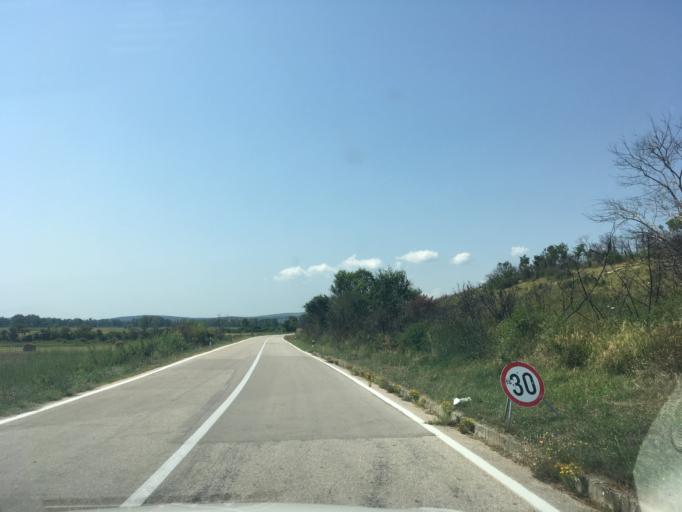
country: HR
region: Sibensko-Kniniska
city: Zaton
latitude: 43.9349
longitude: 15.7943
